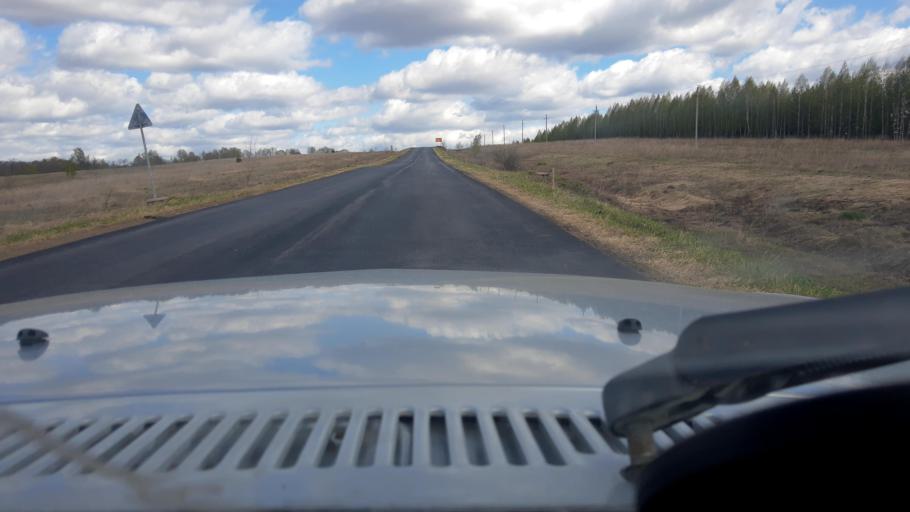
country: RU
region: Bashkortostan
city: Pavlovka
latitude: 55.3583
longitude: 56.4087
